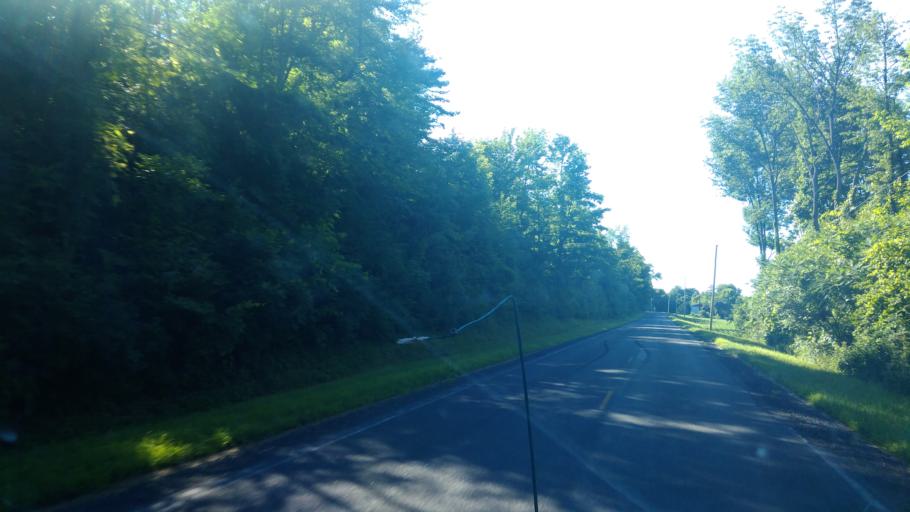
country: US
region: New York
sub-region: Wayne County
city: Lyons
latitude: 43.0077
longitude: -76.9738
